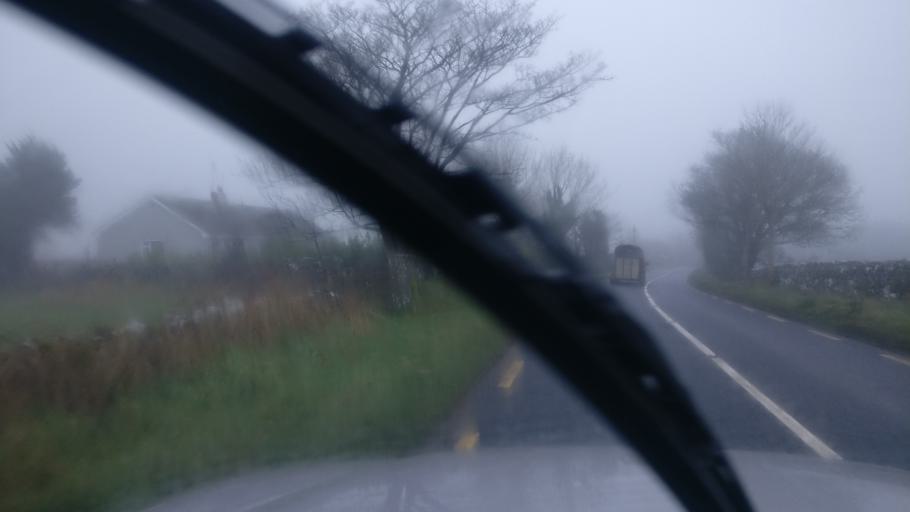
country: IE
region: Connaught
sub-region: County Galway
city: Loughrea
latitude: 53.1642
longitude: -8.6783
